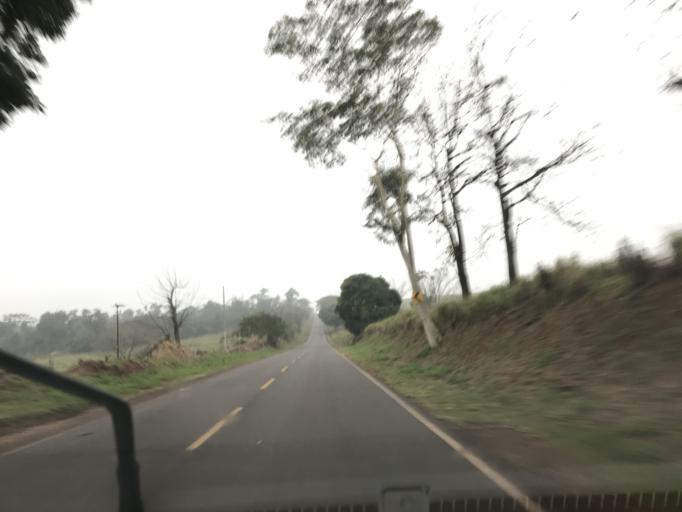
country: PY
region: Canindeyu
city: Salto del Guaira
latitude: -24.0943
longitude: -54.0969
